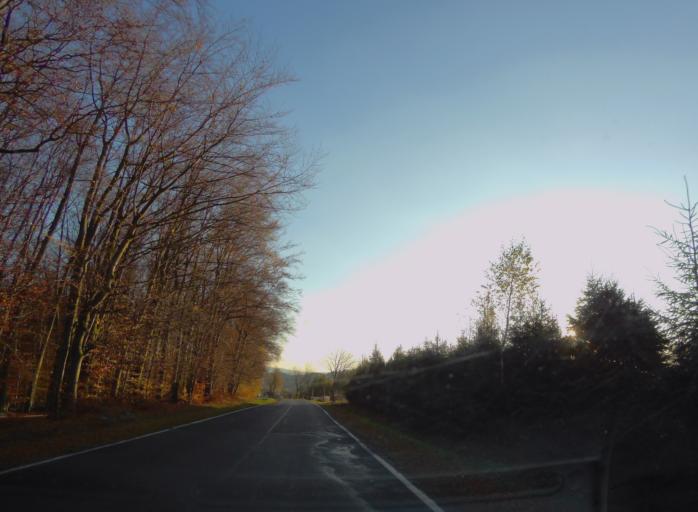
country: PL
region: Subcarpathian Voivodeship
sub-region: Powiat leski
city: Polanczyk
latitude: 49.3854
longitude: 22.4298
